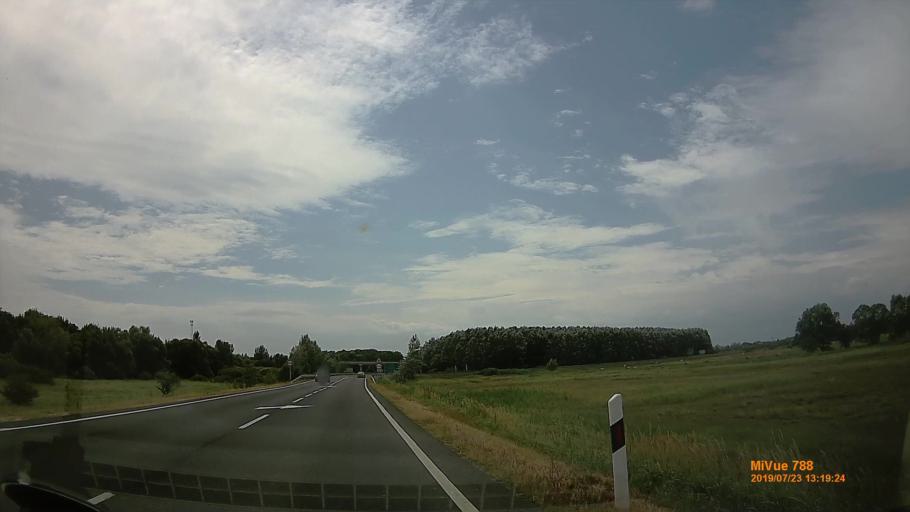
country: HU
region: Hajdu-Bihar
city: Polgar
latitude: 47.8744
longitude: 21.1406
